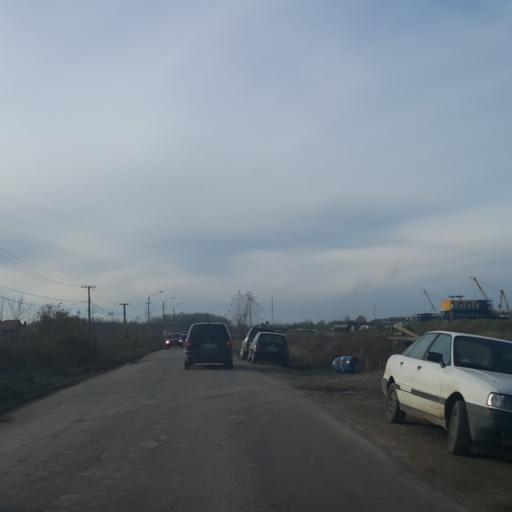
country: RS
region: Central Serbia
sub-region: Belgrade
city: Lazarevac
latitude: 44.4008
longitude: 20.3619
